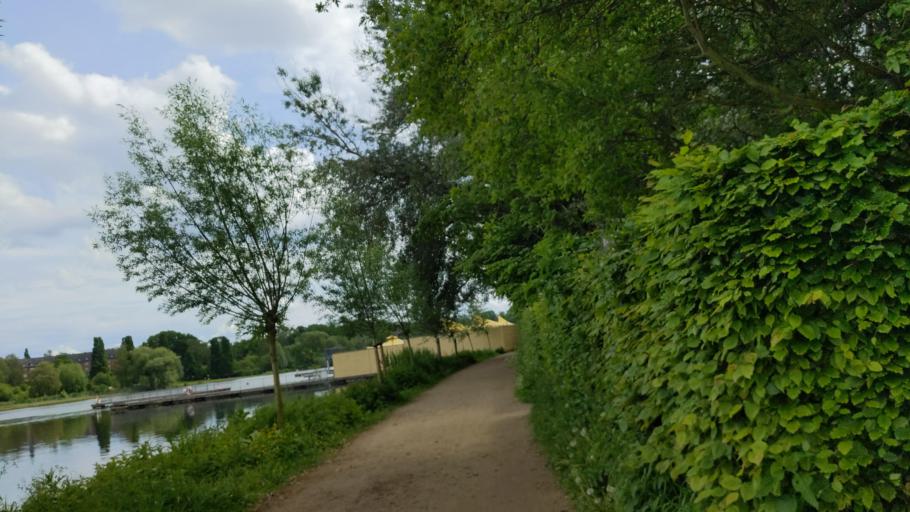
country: DE
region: Schleswig-Holstein
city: Luebeck
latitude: 53.8705
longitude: 10.7037
